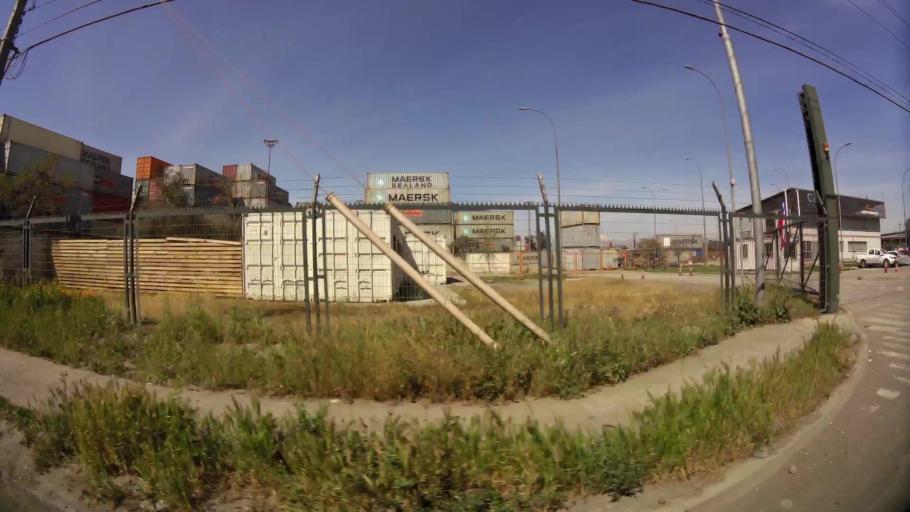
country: CL
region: Santiago Metropolitan
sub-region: Provincia de Maipo
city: San Bernardo
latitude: -33.5411
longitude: -70.6955
